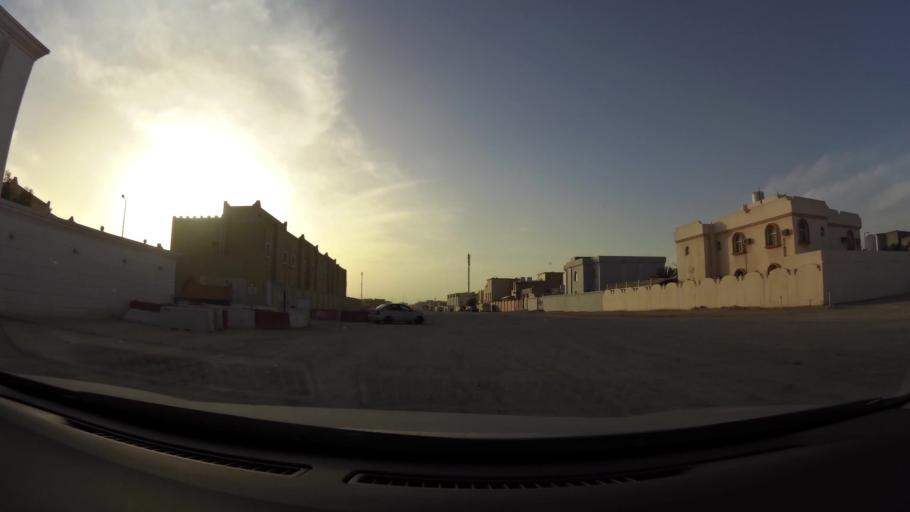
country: QA
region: Al Wakrah
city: Al Wakrah
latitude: 25.1476
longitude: 51.6098
